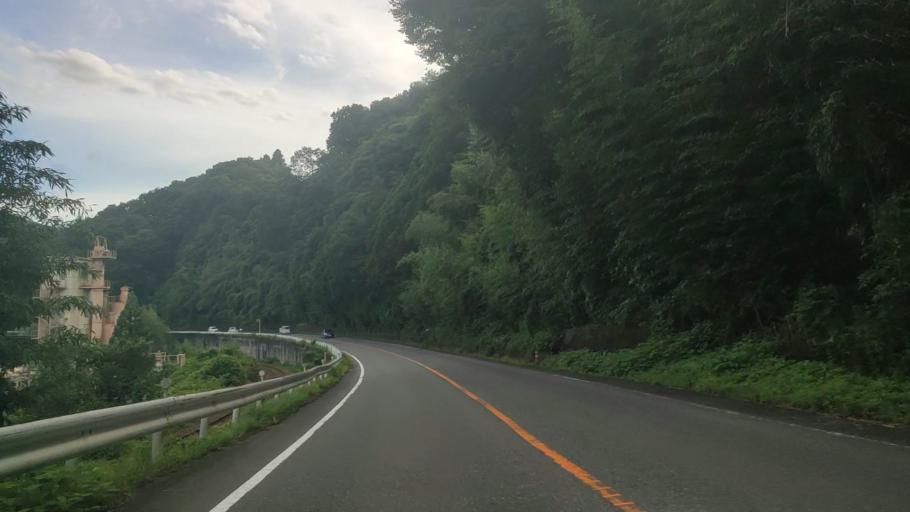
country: JP
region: Gunma
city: Omamacho-omama
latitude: 36.5121
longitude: 139.2972
